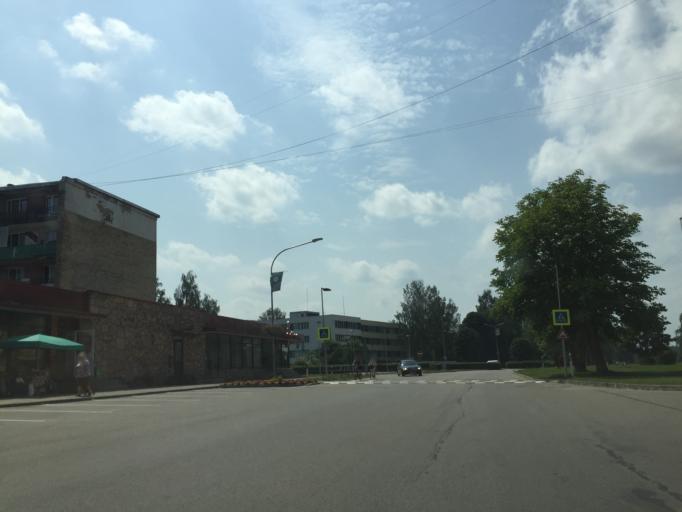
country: LV
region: Olaine
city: Olaine
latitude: 56.7838
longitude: 23.9357
